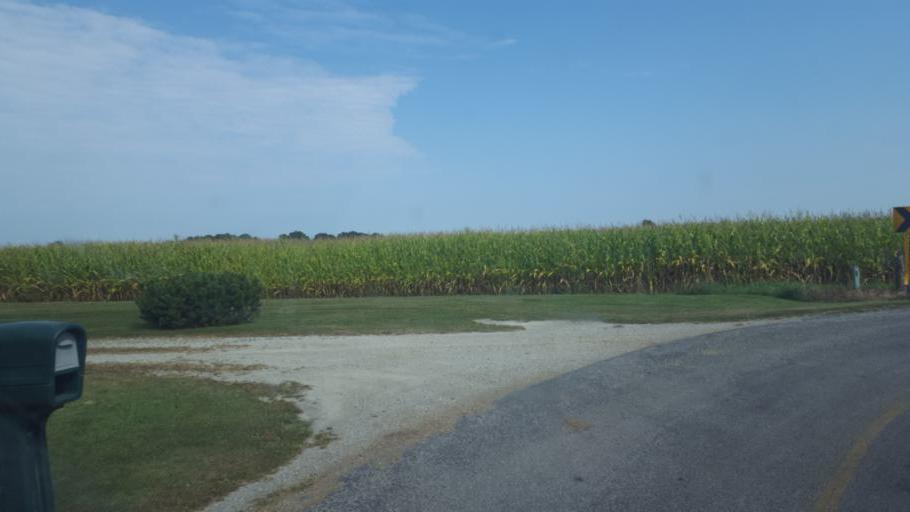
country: US
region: Ohio
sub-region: Delaware County
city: Ashley
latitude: 40.4855
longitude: -83.0068
